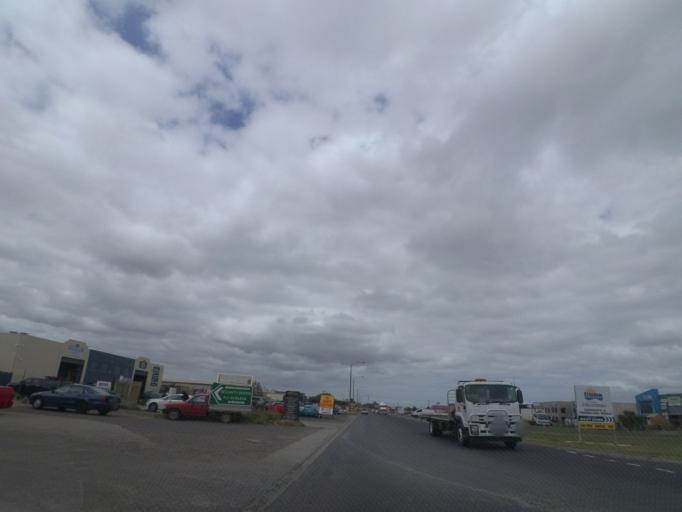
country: AU
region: Victoria
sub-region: Brimbank
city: Deer Park
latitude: -37.7672
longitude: 144.7533
